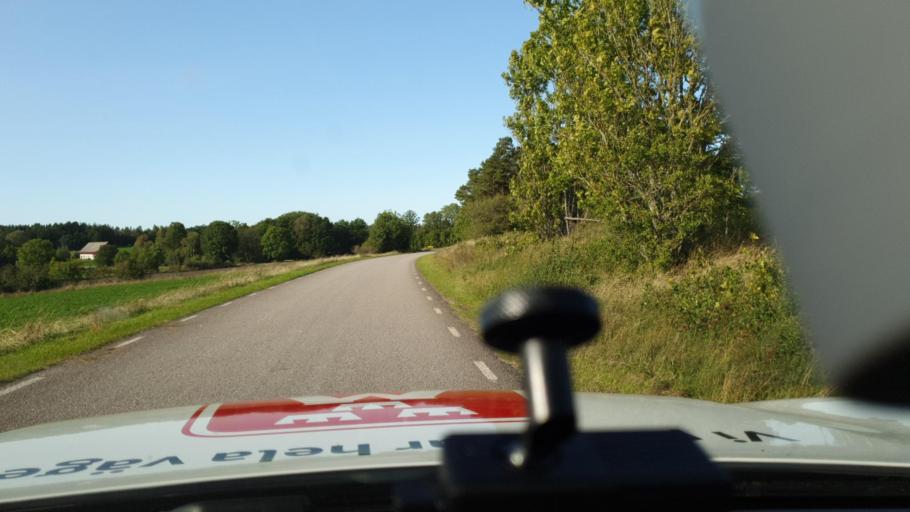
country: SE
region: Gotland
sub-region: Gotland
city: Slite
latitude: 57.6962
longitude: 18.6319
